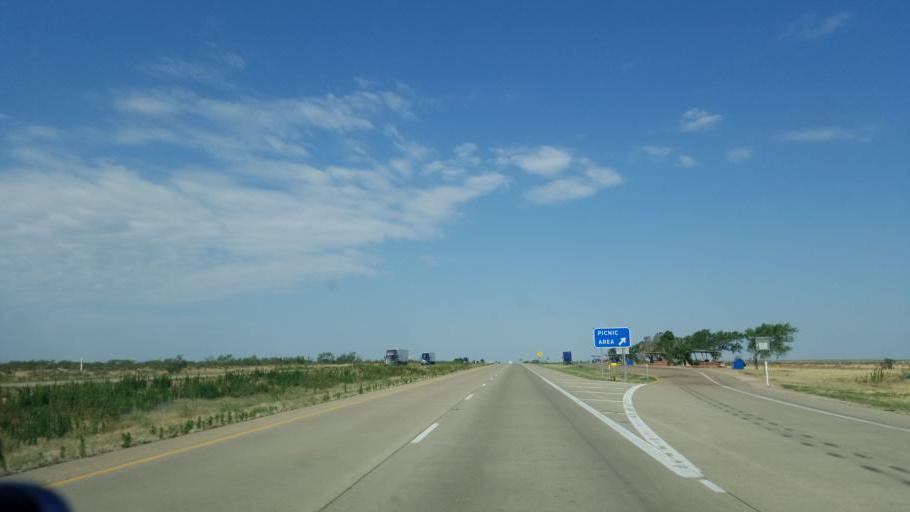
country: US
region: Texas
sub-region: Oldham County
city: Vega
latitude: 35.2412
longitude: -102.8255
